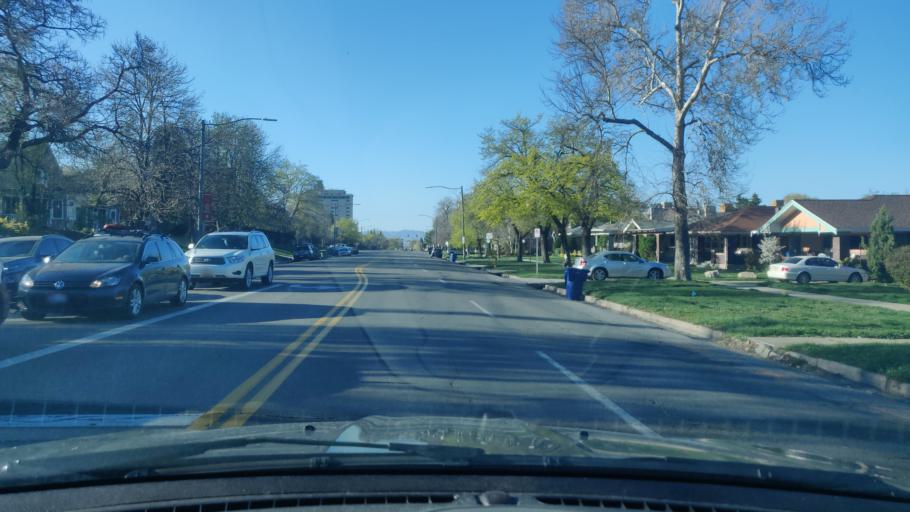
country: US
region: Utah
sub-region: Salt Lake County
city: Salt Lake City
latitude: 40.7627
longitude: -111.8539
